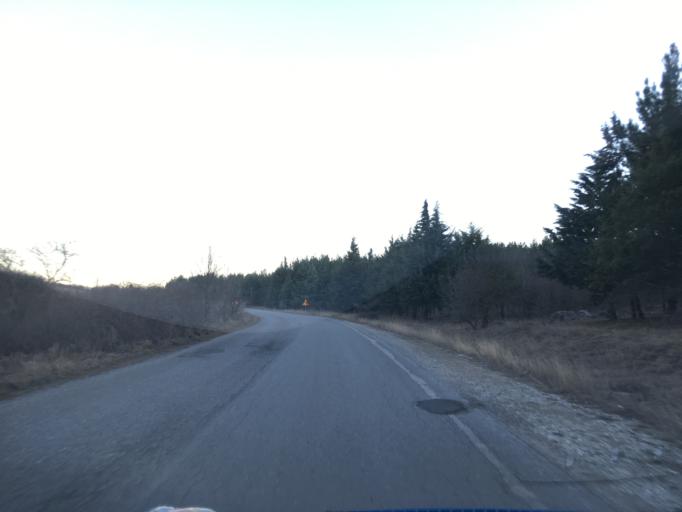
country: GR
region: West Macedonia
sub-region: Nomos Kozanis
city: Koila
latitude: 40.3239
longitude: 21.8142
